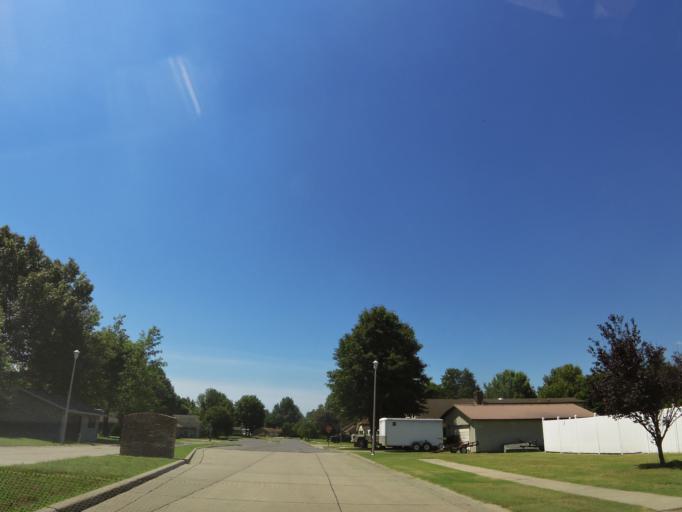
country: US
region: Missouri
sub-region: New Madrid County
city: New Madrid
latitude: 36.5993
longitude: -89.5267
